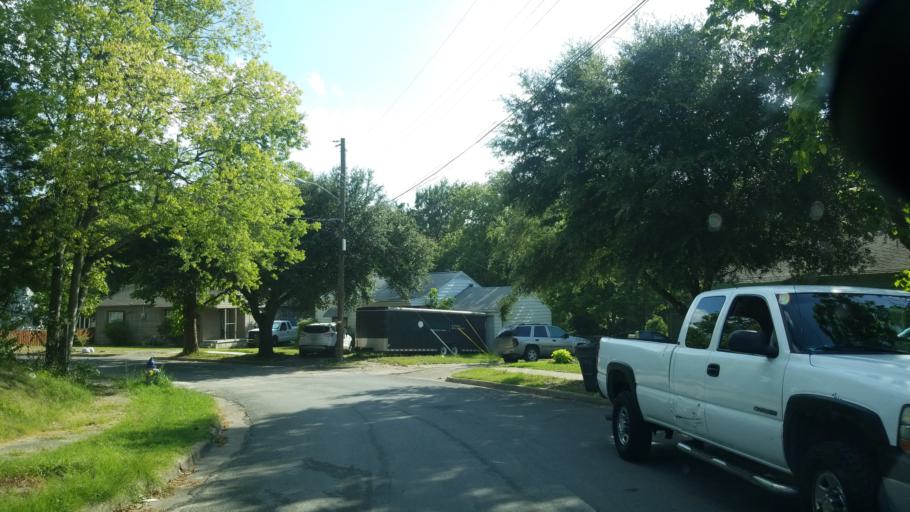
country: US
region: Texas
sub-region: Dallas County
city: Dallas
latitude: 32.7689
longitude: -96.7111
